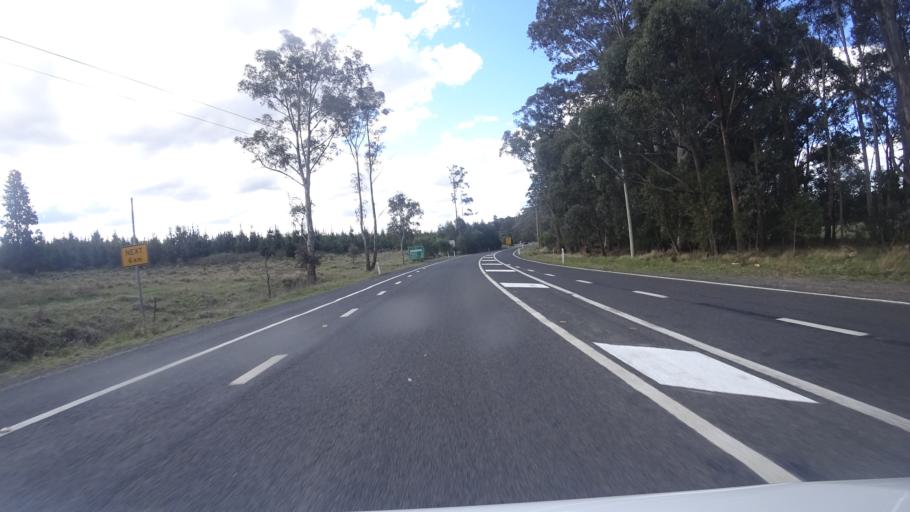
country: AU
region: New South Wales
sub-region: Lithgow
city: Bowenfels
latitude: -33.6765
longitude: 150.0507
